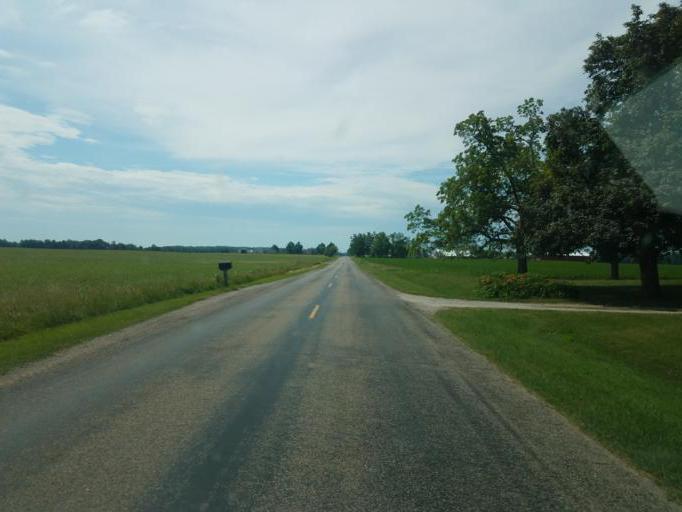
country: US
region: Michigan
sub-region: Barry County
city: Nashville
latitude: 42.6564
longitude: -84.9952
